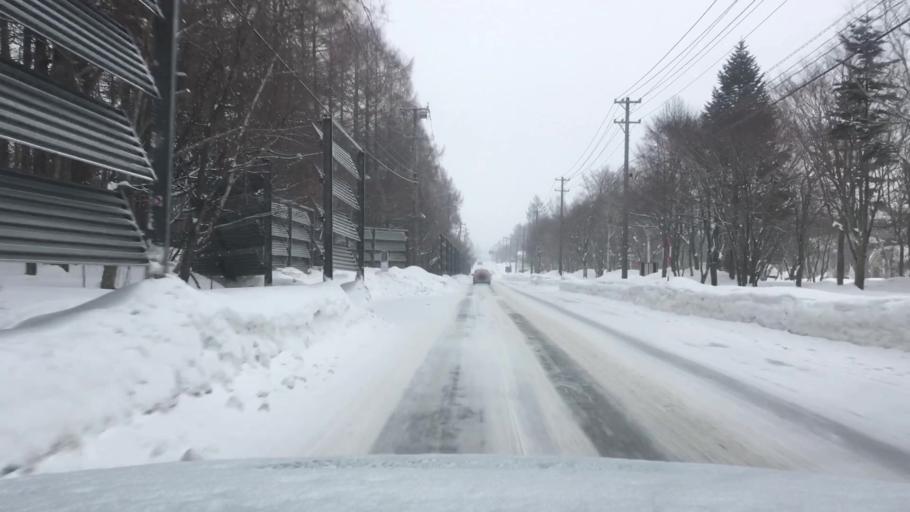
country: JP
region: Akita
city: Hanawa
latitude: 40.0072
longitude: 140.9744
